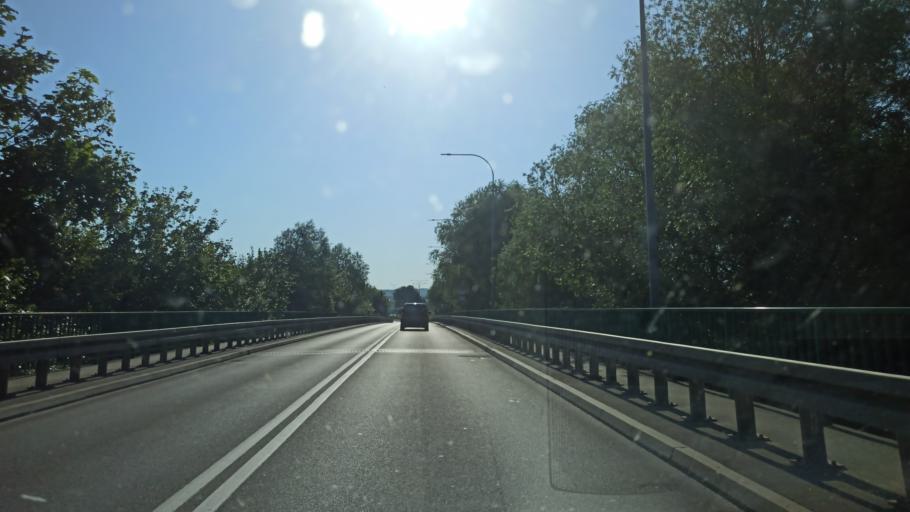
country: PL
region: Warmian-Masurian Voivodeship
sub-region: Powiat elblaski
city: Elblag
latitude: 54.1664
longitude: 19.3716
